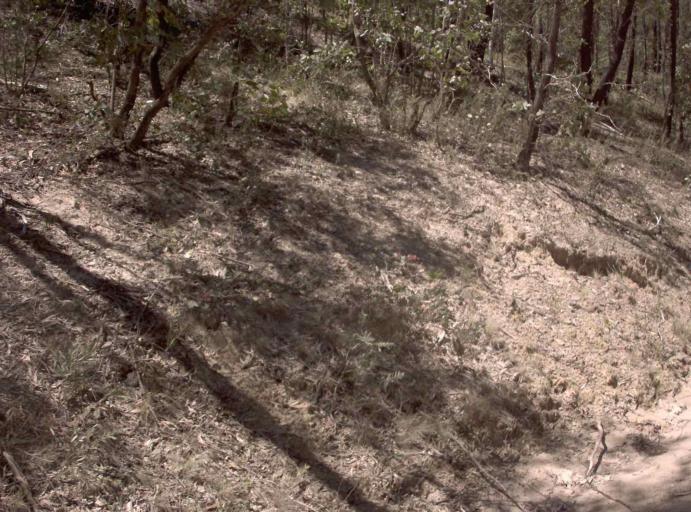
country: AU
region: New South Wales
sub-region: Snowy River
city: Jindabyne
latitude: -37.0708
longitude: 148.3239
